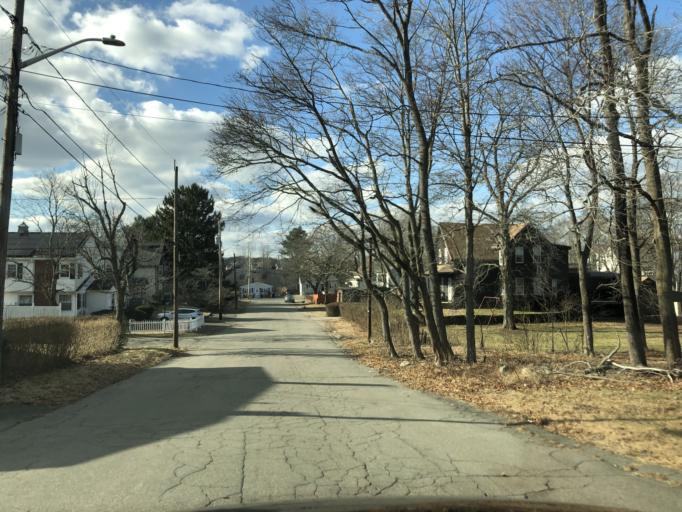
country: US
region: Massachusetts
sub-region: Plymouth County
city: Brockton
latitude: 42.1089
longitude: -71.0173
